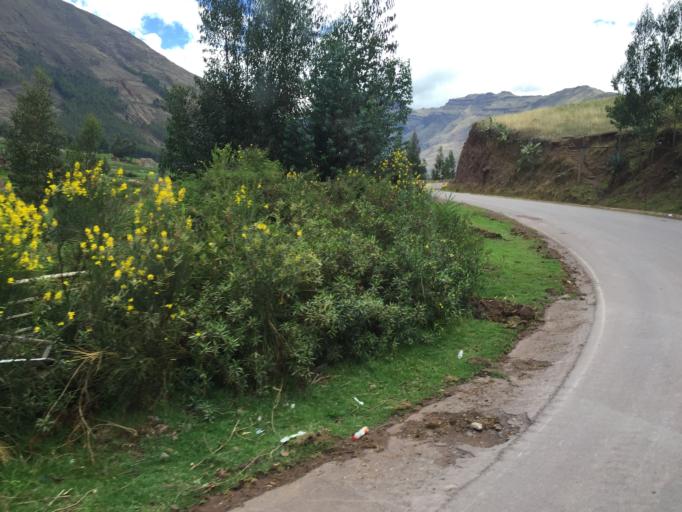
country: PE
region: Cusco
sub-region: Provincia de Calca
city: Pisac
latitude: -13.4059
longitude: -71.8314
